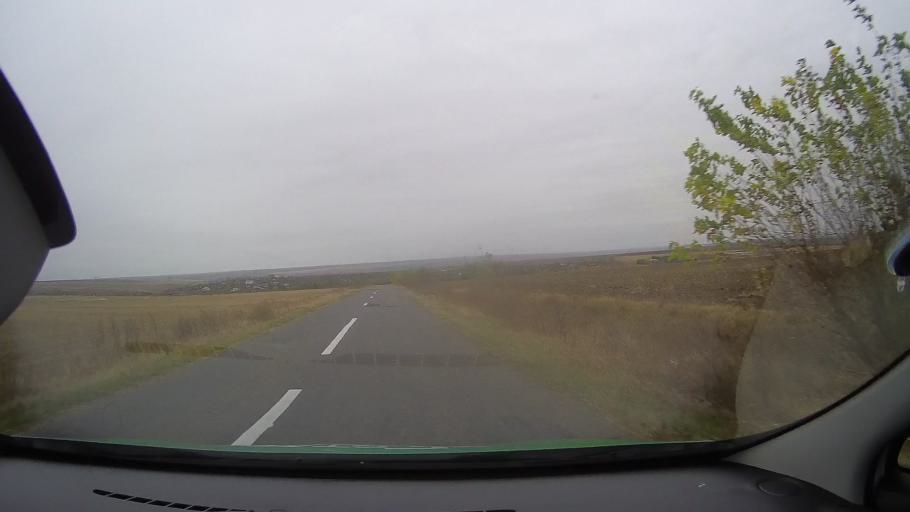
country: RO
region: Constanta
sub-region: Comuna Vulturu
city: Vulturu
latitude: 44.6938
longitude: 28.2423
